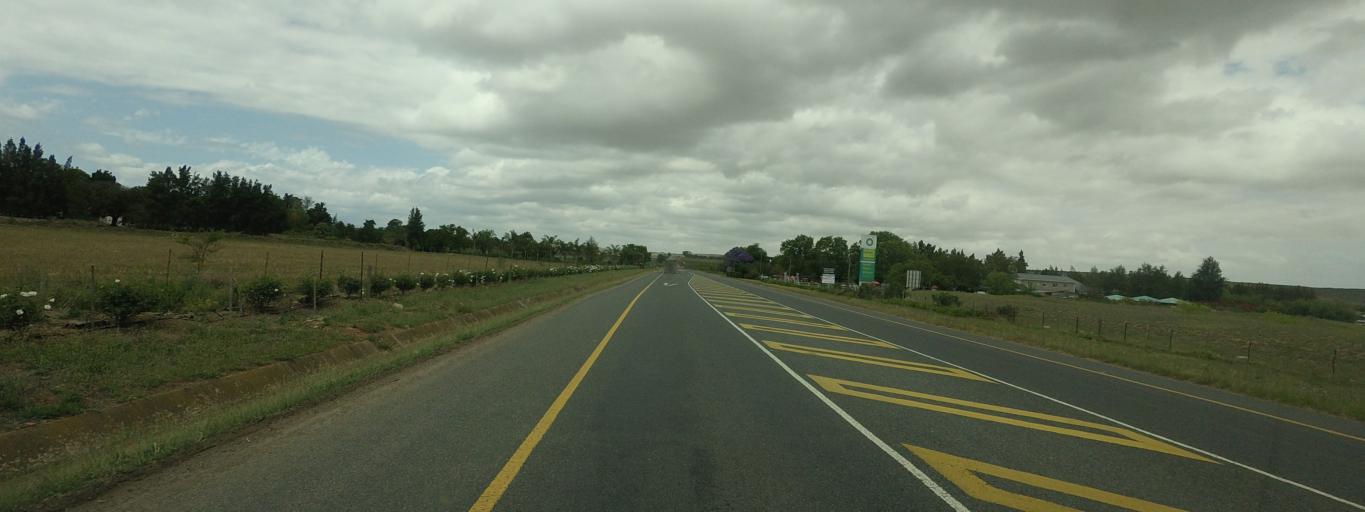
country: ZA
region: Western Cape
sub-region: Overberg District Municipality
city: Swellendam
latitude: -34.0378
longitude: 20.5447
